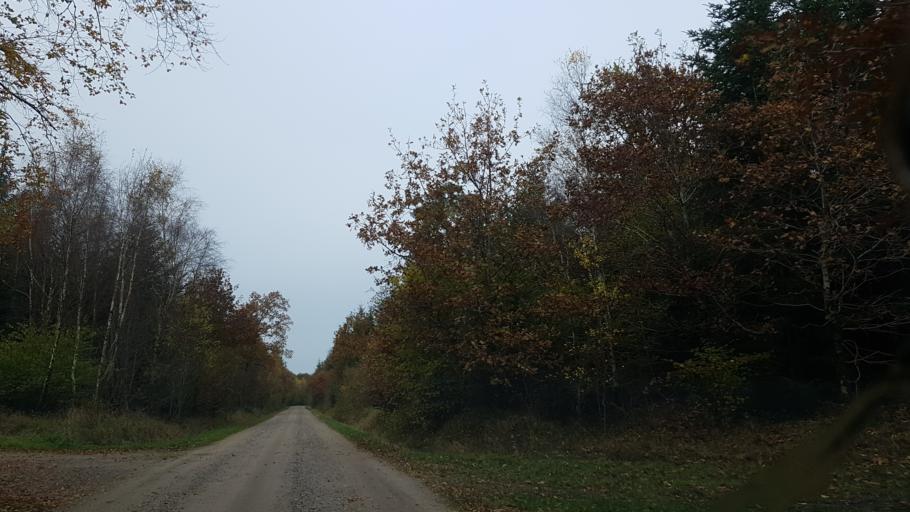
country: DK
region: South Denmark
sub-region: Tonder Kommune
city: Sherrebek
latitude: 55.1883
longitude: 8.7596
